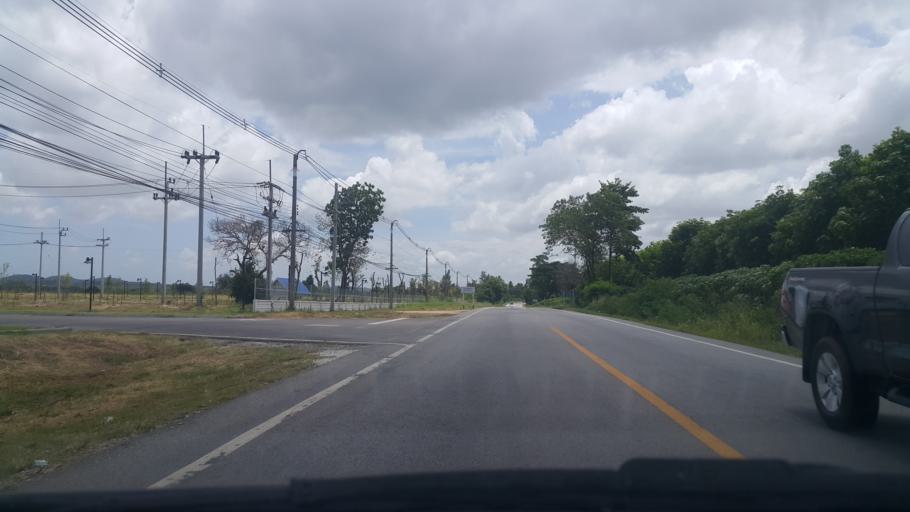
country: TH
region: Rayong
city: Ban Chang
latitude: 12.7786
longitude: 101.0256
